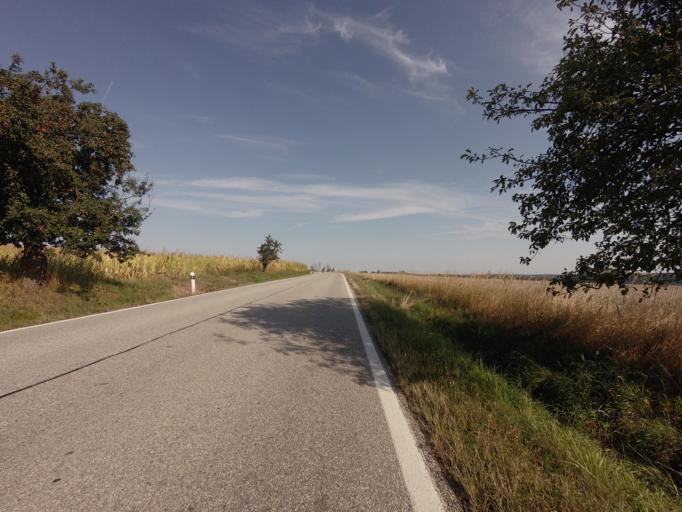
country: CZ
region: Jihocesky
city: Bernartice
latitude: 49.2999
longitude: 14.3846
